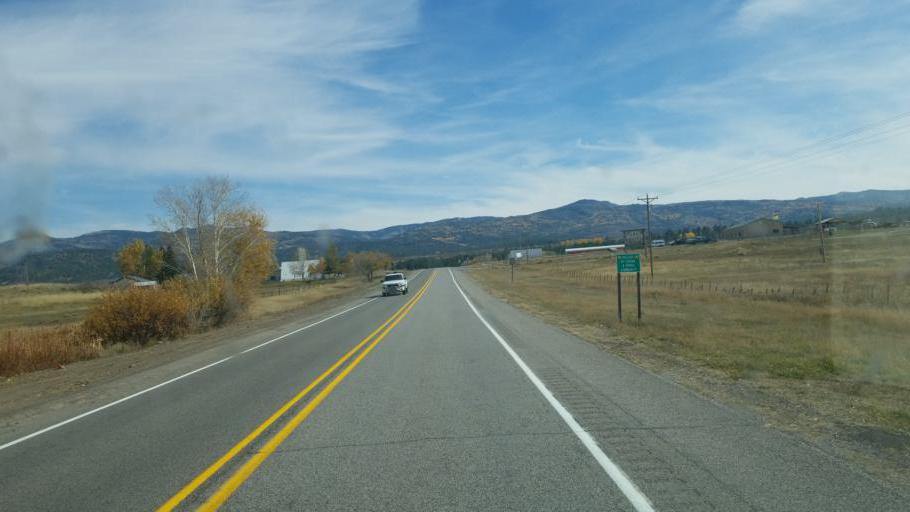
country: US
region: New Mexico
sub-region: Rio Arriba County
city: Chama
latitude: 36.8831
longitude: -106.5946
